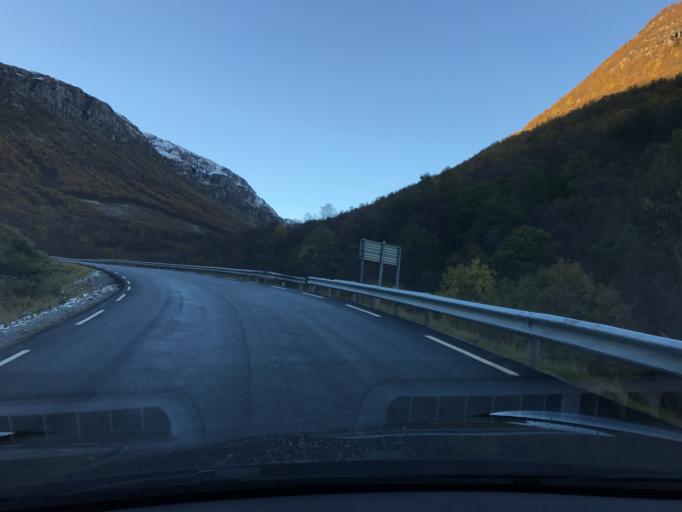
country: NO
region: Sogn og Fjordane
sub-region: Aurland
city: Aurlandsvangen
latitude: 60.8495
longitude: 7.3102
